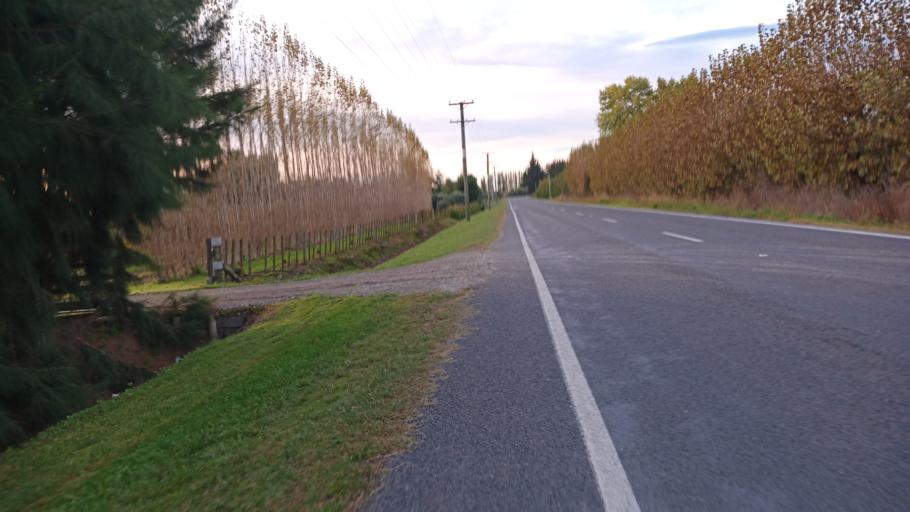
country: NZ
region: Gisborne
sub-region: Gisborne District
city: Gisborne
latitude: -38.6491
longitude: 177.9484
